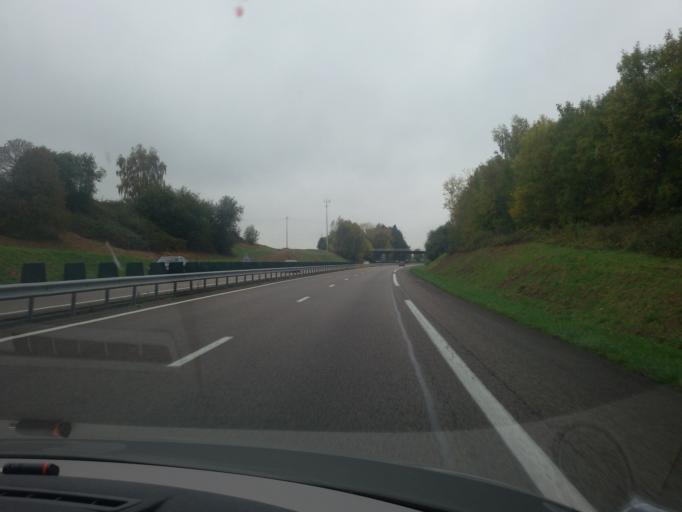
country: FR
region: Haute-Normandie
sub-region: Departement de l'Eure
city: Pont-Audemer
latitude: 49.3912
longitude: 0.5159
